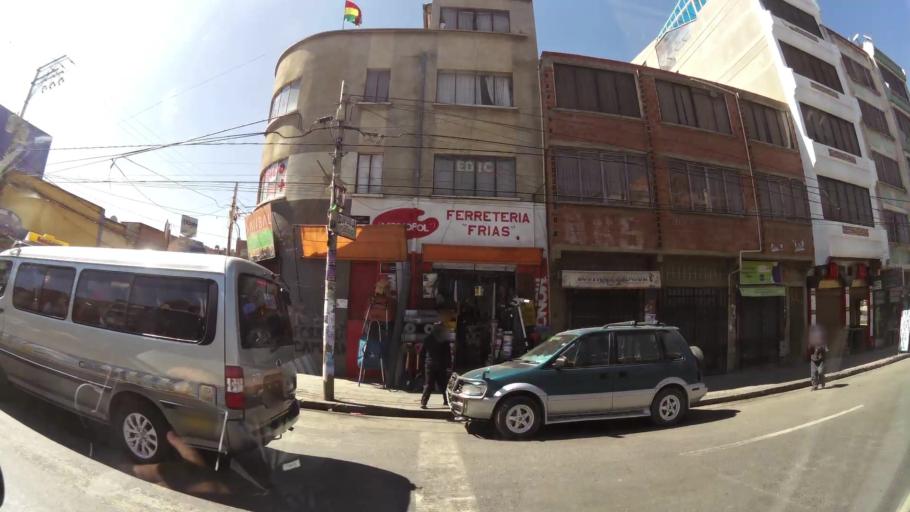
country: BO
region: La Paz
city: La Paz
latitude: -16.4988
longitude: -68.1747
